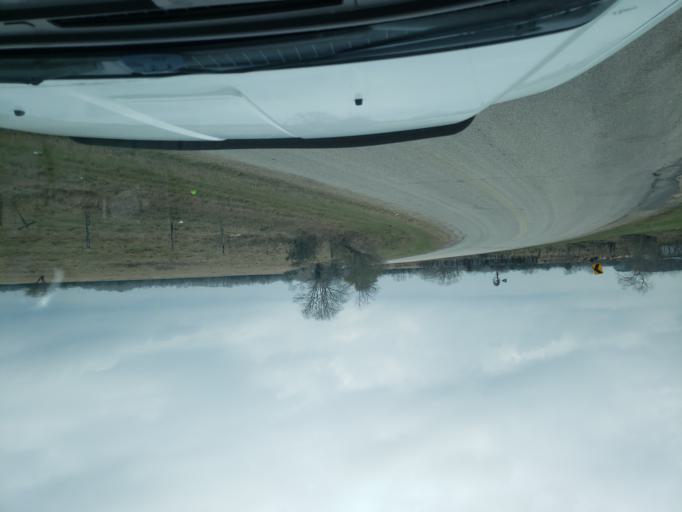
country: US
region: Texas
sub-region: Fort Bend County
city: Needville
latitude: 29.3679
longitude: -95.7265
